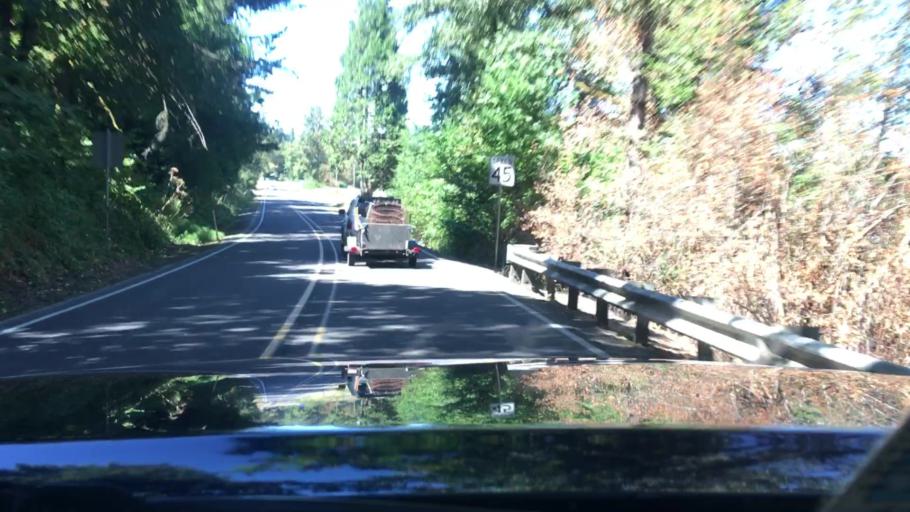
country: US
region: Oregon
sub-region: Lane County
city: Cottage Grove
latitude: 43.8273
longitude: -123.0443
